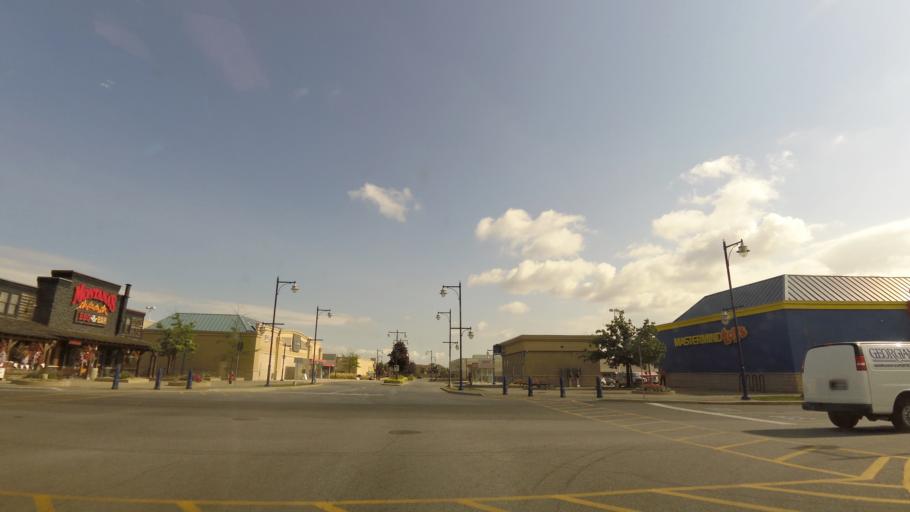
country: CA
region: Ontario
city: Brampton
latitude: 43.7301
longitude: -79.7647
